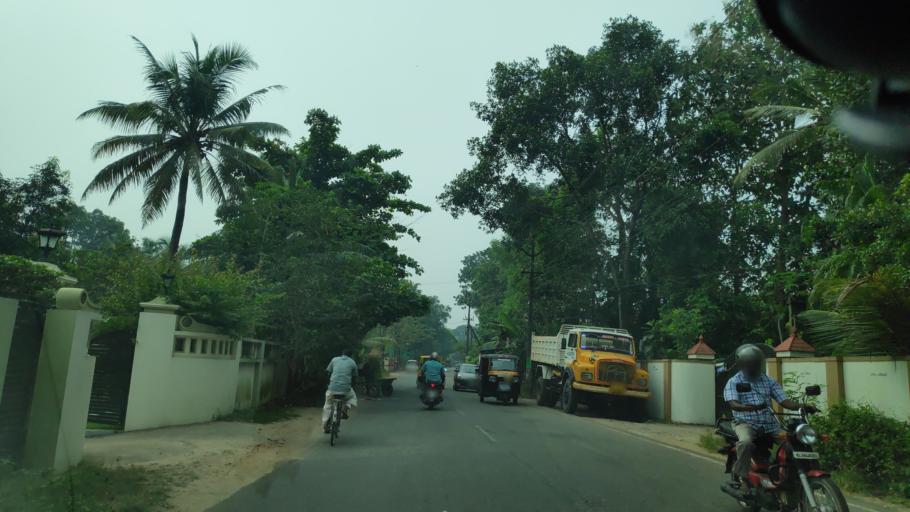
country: IN
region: Kerala
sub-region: Alappuzha
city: Alleppey
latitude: 9.5788
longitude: 76.3490
